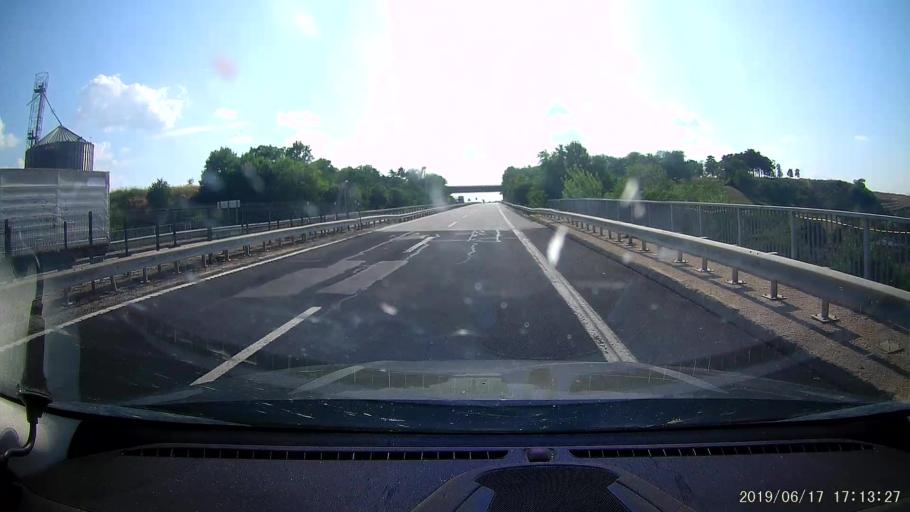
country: TR
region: Edirne
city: Edirne
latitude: 41.7008
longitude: 26.5397
